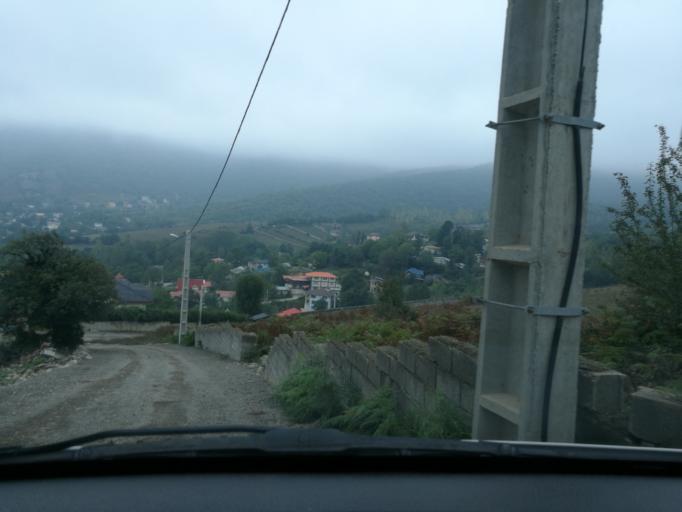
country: IR
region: Mazandaran
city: `Abbasabad
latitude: 36.4981
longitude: 51.2056
